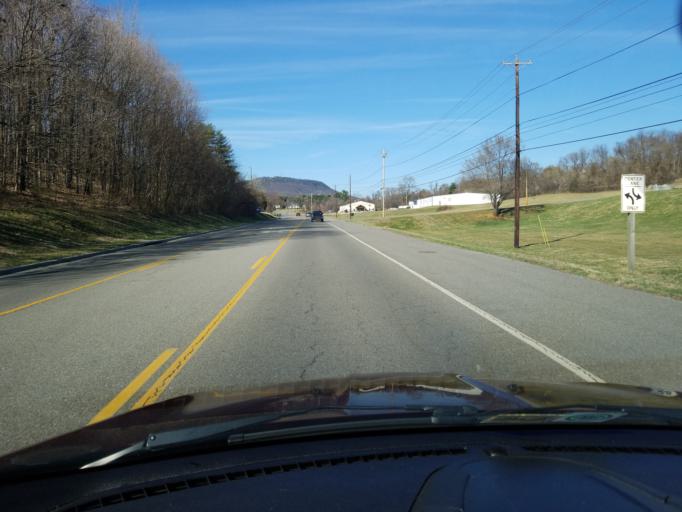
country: US
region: Virginia
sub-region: Roanoke County
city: Hollins
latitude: 37.3331
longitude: -79.9267
